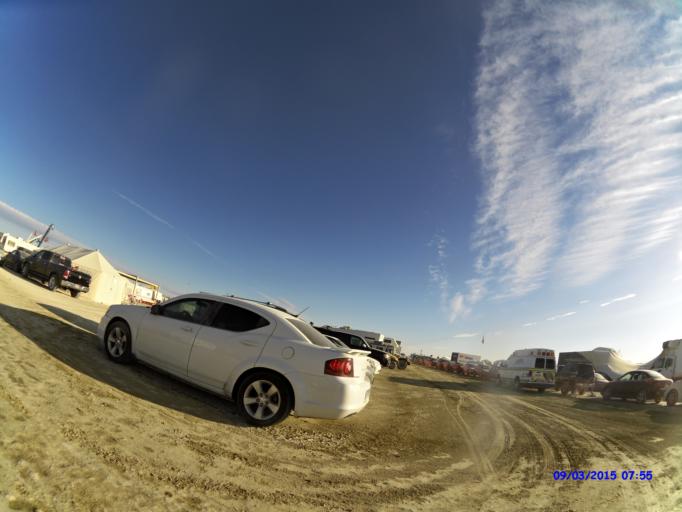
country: US
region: Nevada
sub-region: Pershing County
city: Lovelock
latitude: 40.7789
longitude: -119.2105
